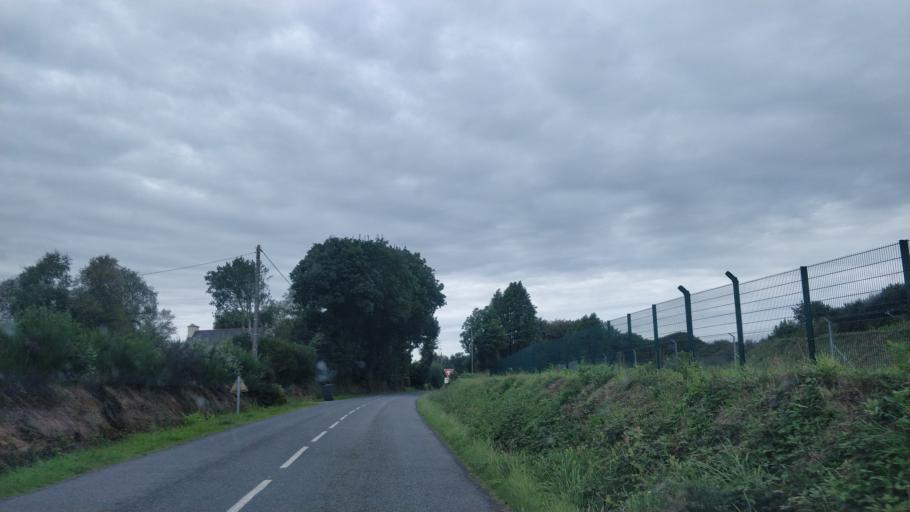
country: FR
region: Brittany
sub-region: Departement du Finistere
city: La Forest-Landerneau
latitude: 48.4011
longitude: -4.3168
